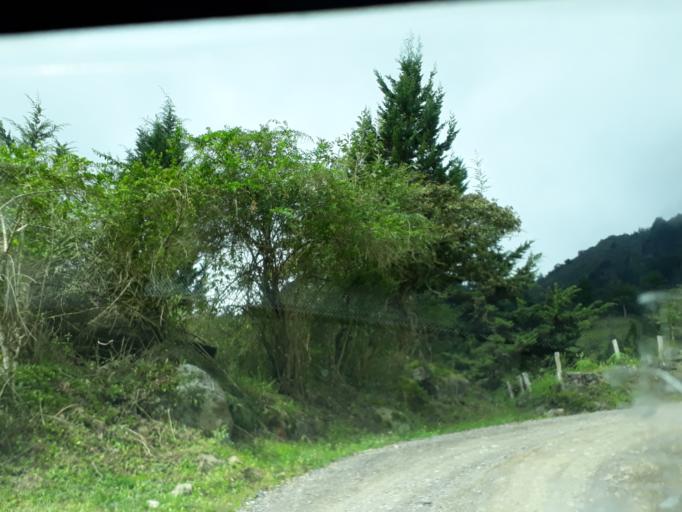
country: CO
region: Cundinamarca
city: Carmen de Carupa
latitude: 5.3806
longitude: -73.9788
